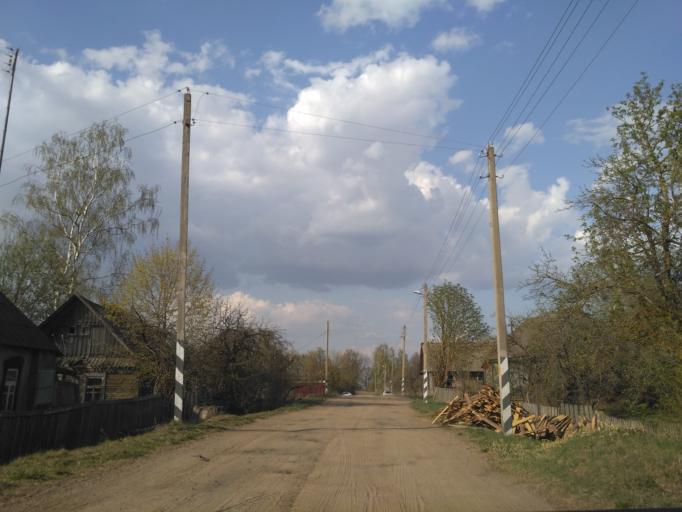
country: BY
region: Minsk
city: Khalopyenichy
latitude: 54.5035
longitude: 28.8484
